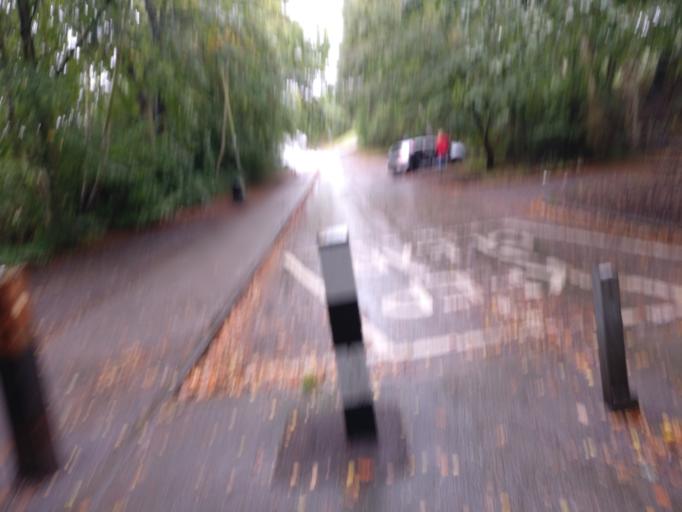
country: GB
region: England
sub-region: Surrey
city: Frimley
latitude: 51.3198
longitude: -0.7220
